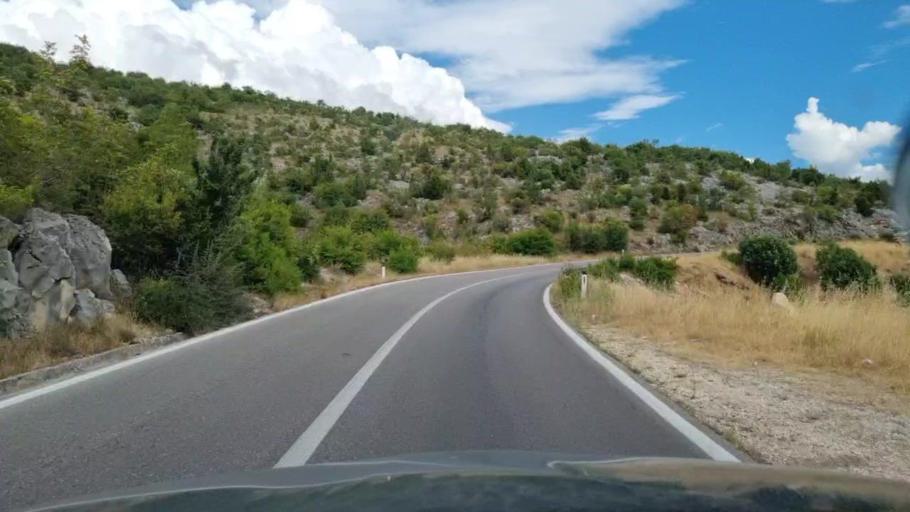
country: BA
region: Federation of Bosnia and Herzegovina
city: Blagaj
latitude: 43.2668
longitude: 17.8927
